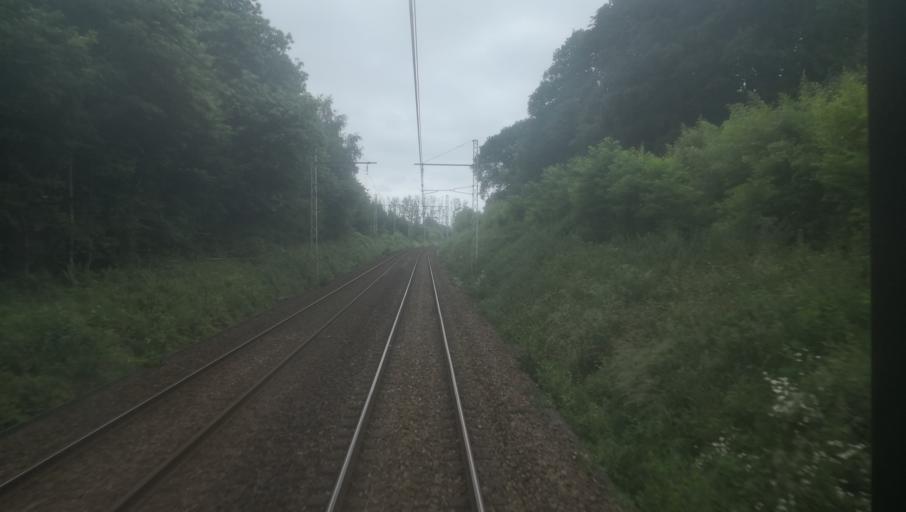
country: FR
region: Centre
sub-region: Departement de l'Indre
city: Chantome
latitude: 46.4329
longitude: 1.5554
